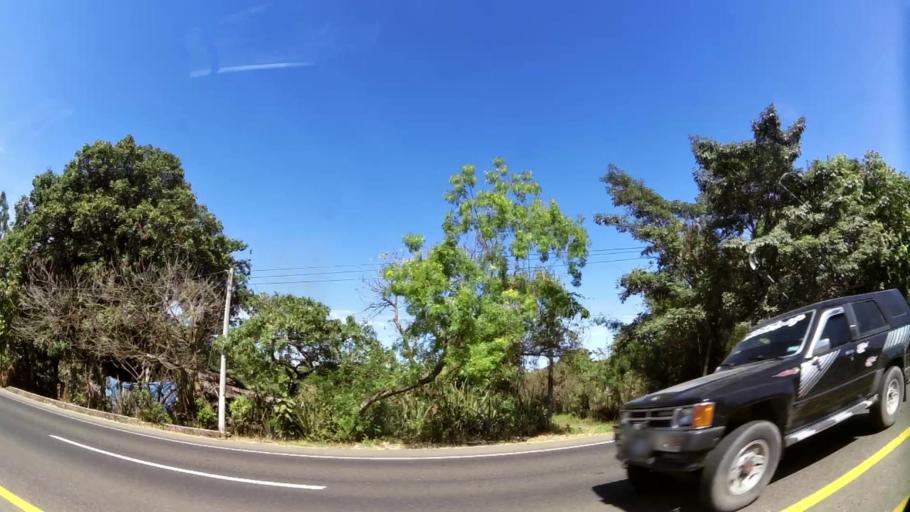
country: SV
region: Ahuachapan
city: Atiquizaya
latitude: 13.9713
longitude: -89.7437
